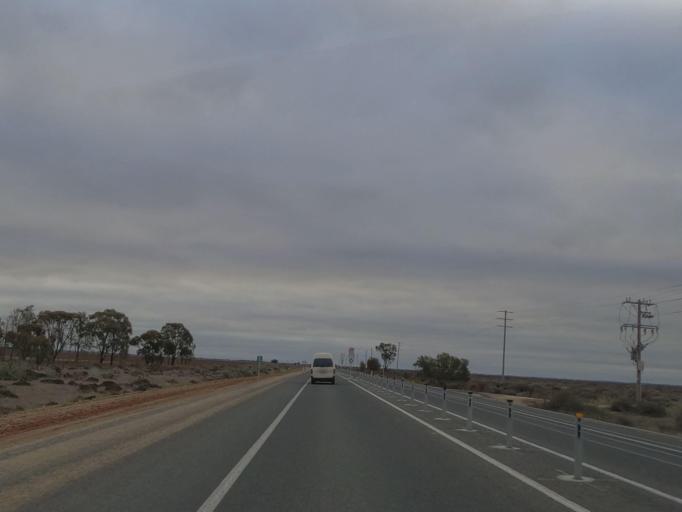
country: AU
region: Victoria
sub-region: Swan Hill
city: Swan Hill
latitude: -35.5182
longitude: 143.7296
